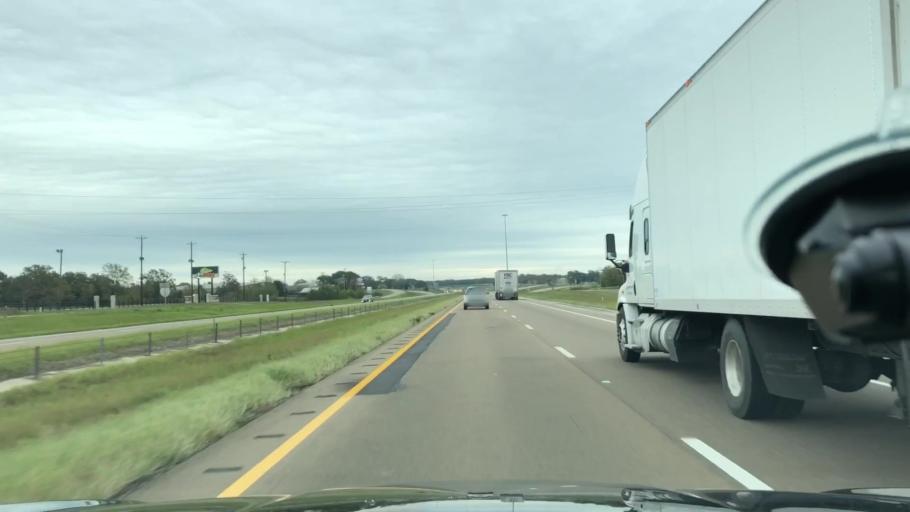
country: US
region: Texas
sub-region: Titus County
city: Mount Pleasant
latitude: 33.1946
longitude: -94.9285
